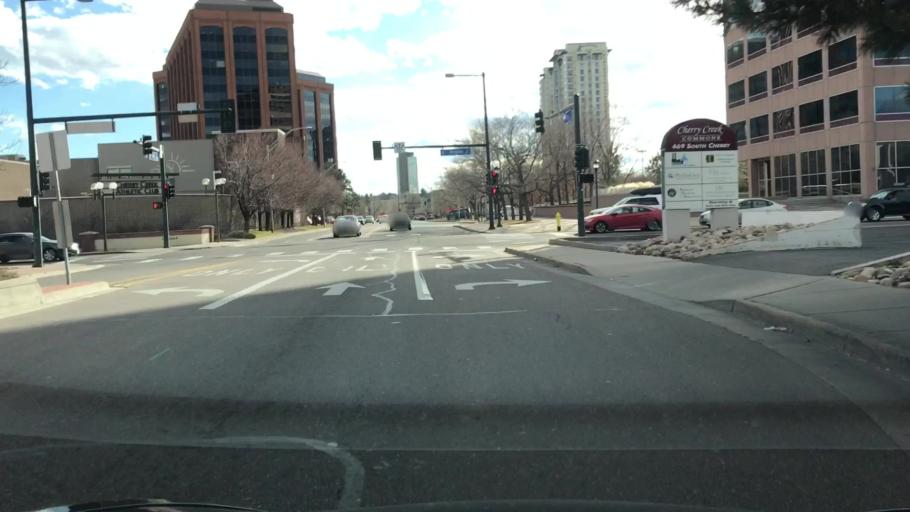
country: US
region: Colorado
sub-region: Arapahoe County
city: Glendale
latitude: 39.7079
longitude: -104.9335
